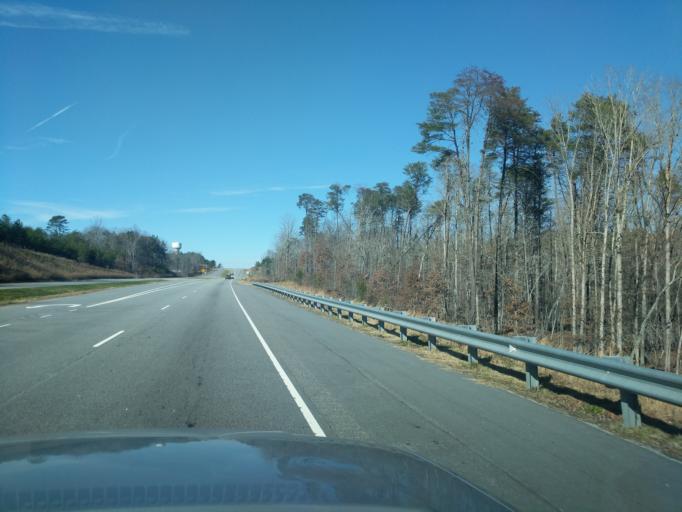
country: US
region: North Carolina
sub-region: Rutherford County
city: Forest City
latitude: 35.2515
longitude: -81.8743
